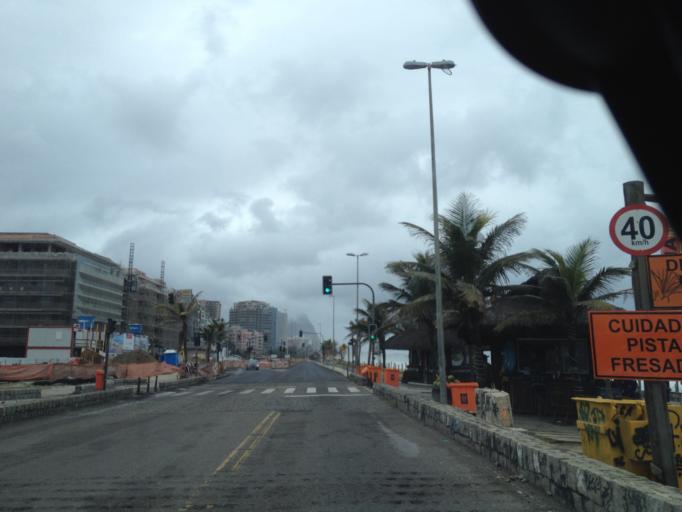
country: BR
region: Rio de Janeiro
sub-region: Rio De Janeiro
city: Rio de Janeiro
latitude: -23.0114
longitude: -43.3746
